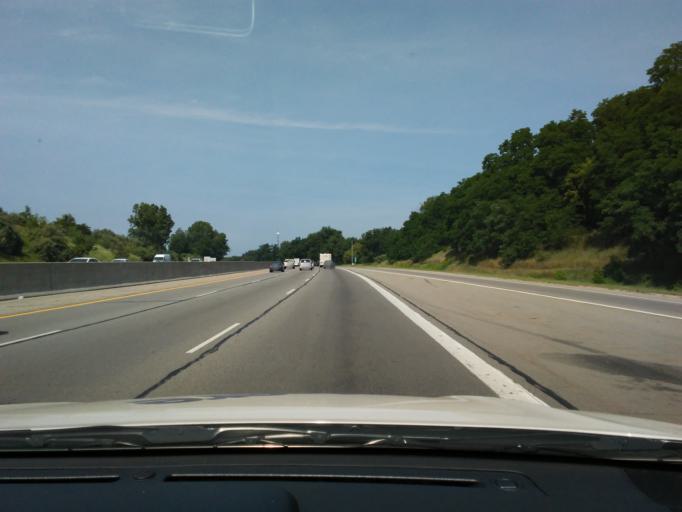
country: US
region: Michigan
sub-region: Oakland County
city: South Lyon
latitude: 42.5205
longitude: -83.6216
